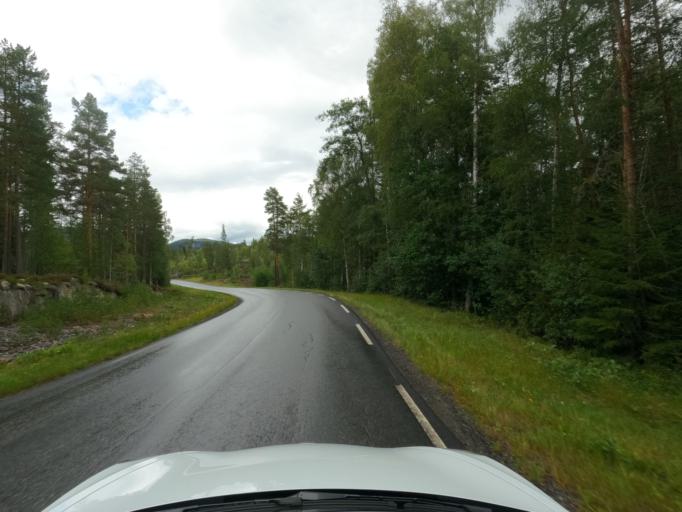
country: NO
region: Telemark
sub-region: Notodden
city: Notodden
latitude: 59.7222
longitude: 9.1654
